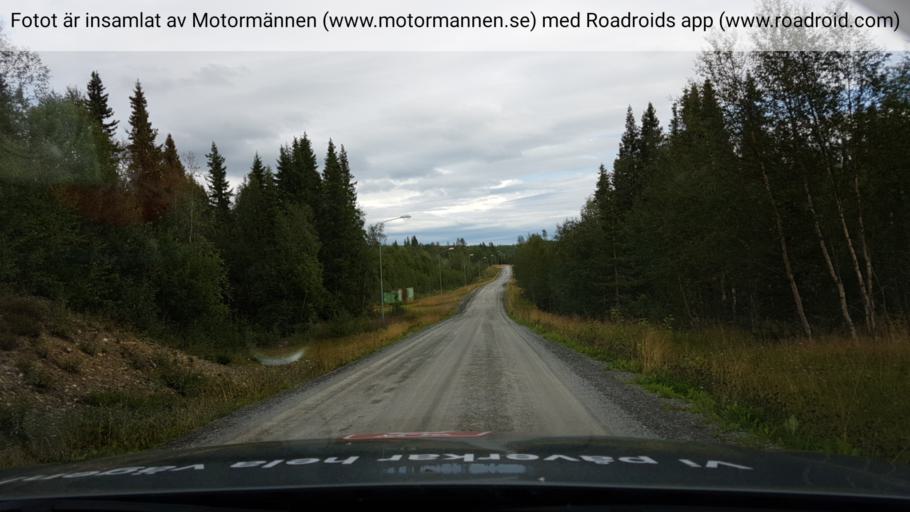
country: SE
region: Jaemtland
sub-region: Krokoms Kommun
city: Valla
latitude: 63.6943
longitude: 13.6526
